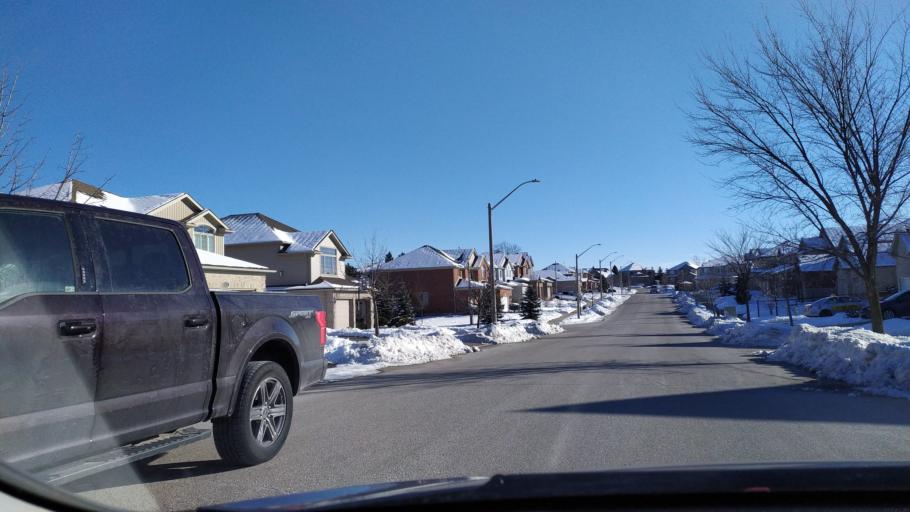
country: CA
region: Ontario
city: Waterloo
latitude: 43.4469
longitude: -80.5652
